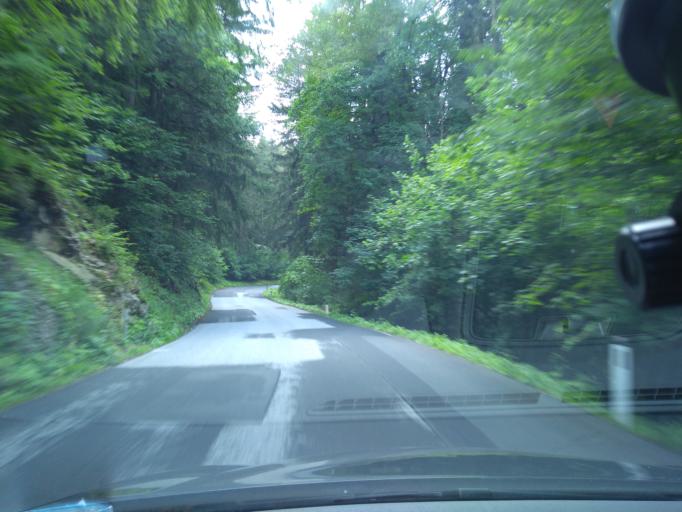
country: AT
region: Styria
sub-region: Politischer Bezirk Graz-Umgebung
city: Semriach
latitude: 47.2318
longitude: 15.4362
